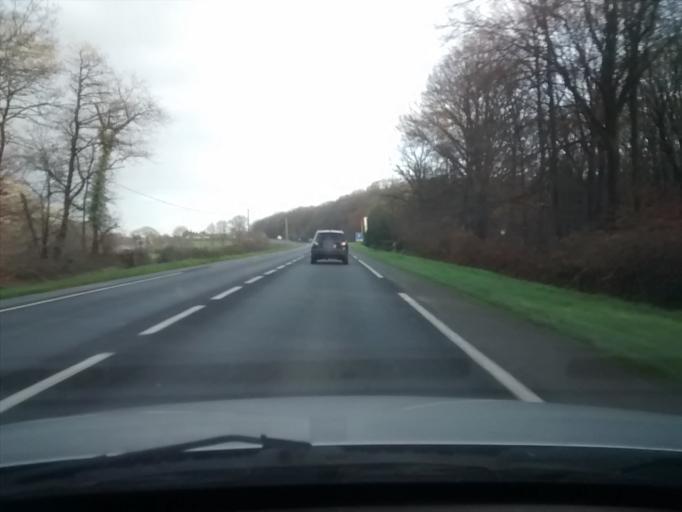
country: FR
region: Pays de la Loire
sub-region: Departement de la Mayenne
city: Port-Brillet
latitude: 48.0759
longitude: -0.9884
